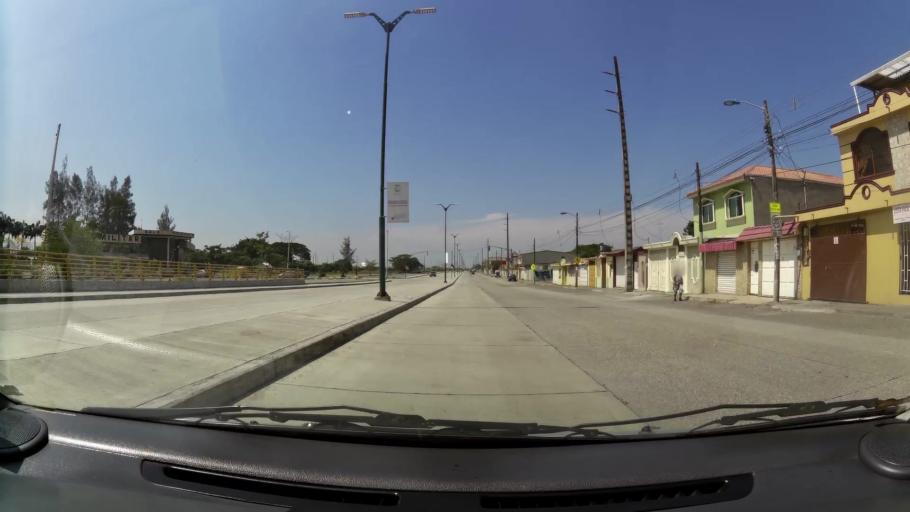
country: EC
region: Guayas
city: Eloy Alfaro
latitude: -2.1089
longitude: -79.9058
